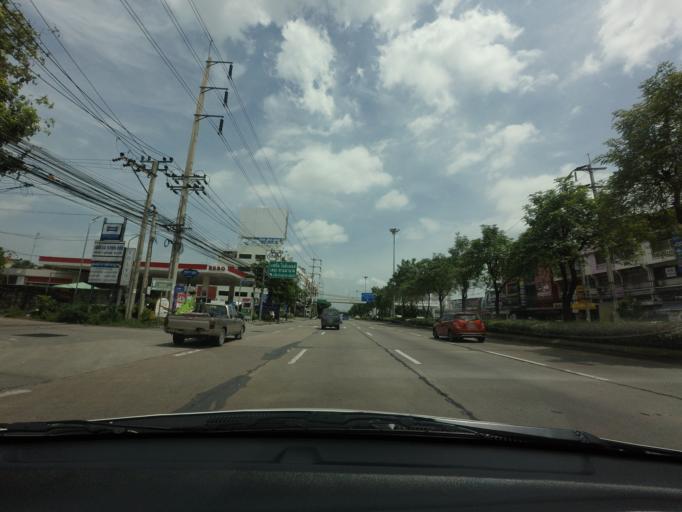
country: TH
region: Bangkok
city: Khan Na Yao
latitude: 13.8319
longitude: 100.6696
